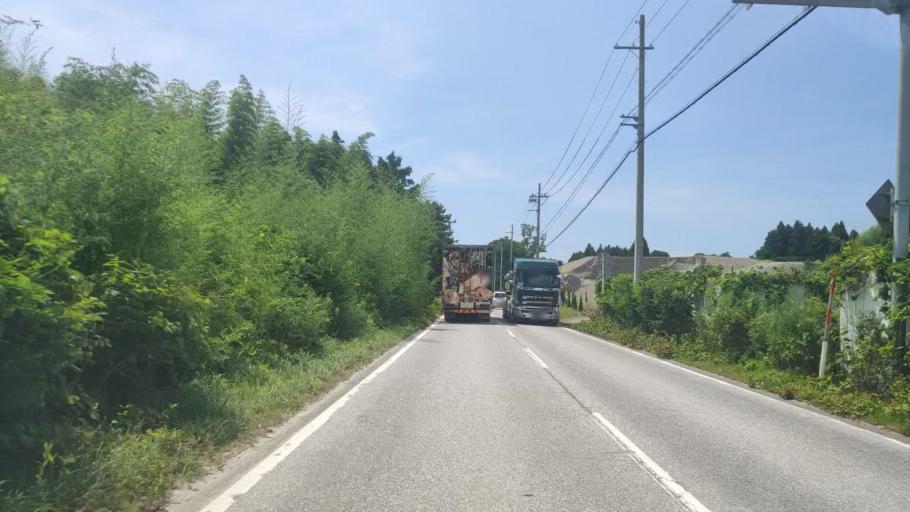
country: JP
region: Shiga Prefecture
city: Nagahama
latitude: 35.3705
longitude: 136.3959
